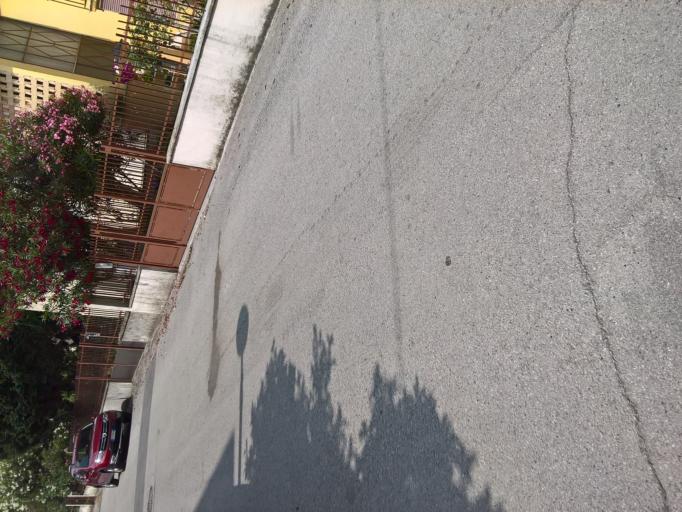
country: IT
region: Veneto
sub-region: Provincia di Padova
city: Battaglia Terme
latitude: 45.2902
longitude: 11.7770
